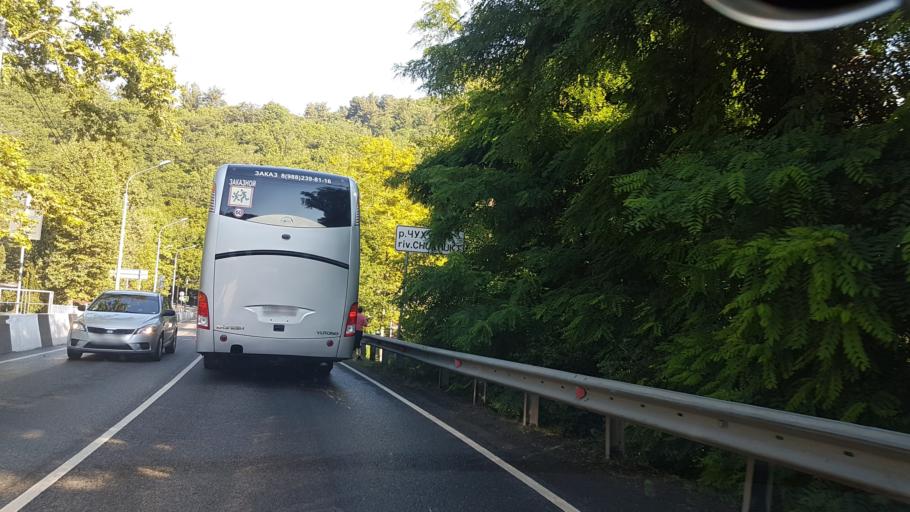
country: RU
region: Krasnodarskiy
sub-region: Sochi City
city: Lazarevskoye
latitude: 43.8539
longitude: 39.4112
